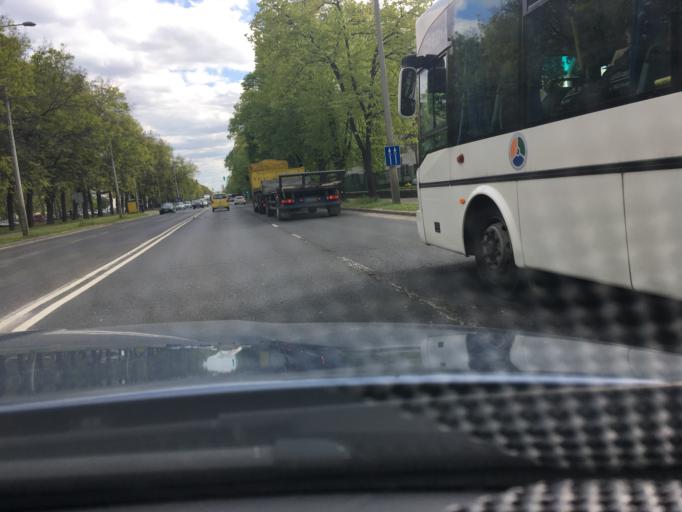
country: HU
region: Hajdu-Bihar
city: Debrecen
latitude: 47.5505
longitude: 21.6097
